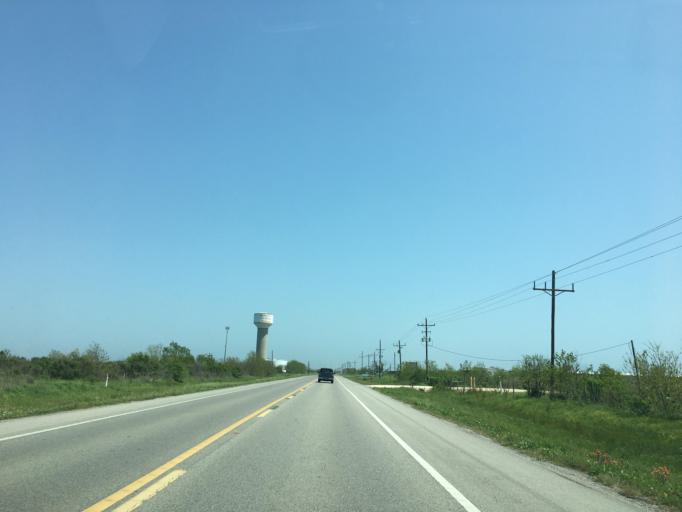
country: US
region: Texas
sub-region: Galveston County
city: Bolivar Peninsula
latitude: 29.4191
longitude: -94.7063
